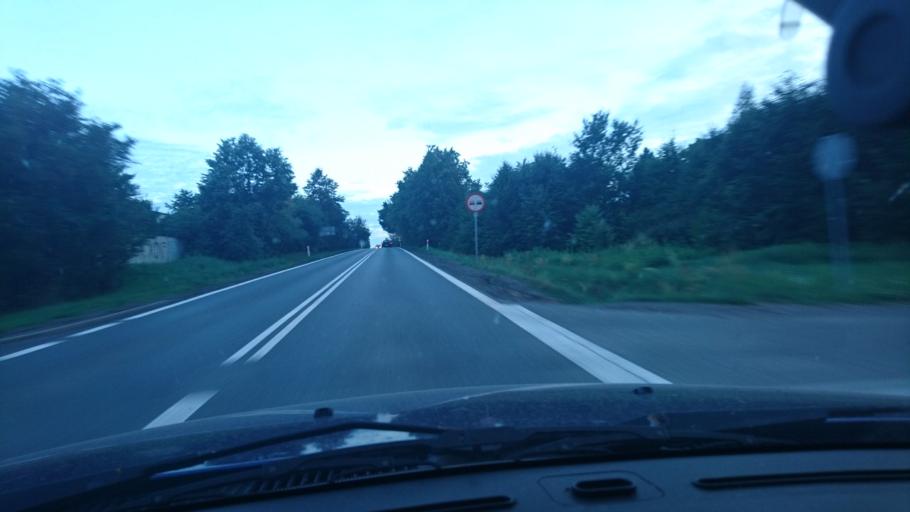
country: PL
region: Silesian Voivodeship
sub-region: Powiat tarnogorski
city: Tarnowskie Gory
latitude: 50.4461
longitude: 18.8364
